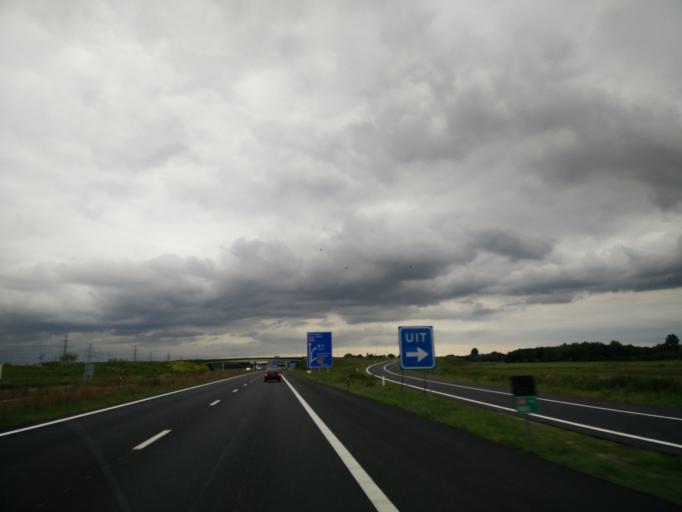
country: NL
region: Drenthe
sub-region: Gemeente Assen
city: Assen
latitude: 52.9534
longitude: 6.5432
